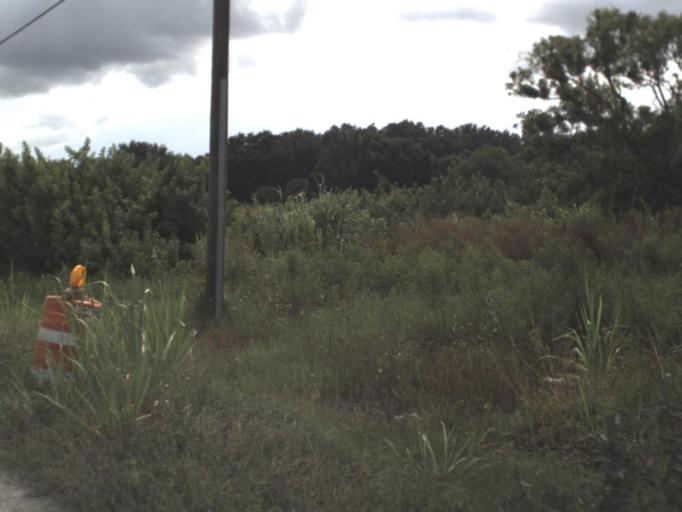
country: US
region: Florida
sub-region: Manatee County
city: Samoset
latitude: 27.4621
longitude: -82.5467
